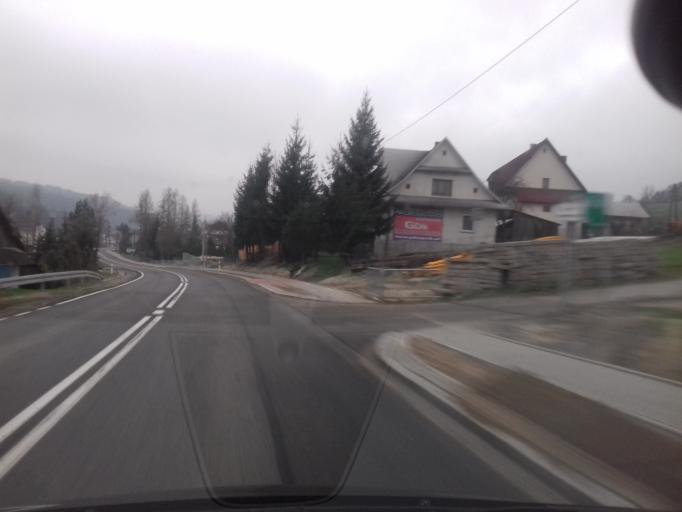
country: PL
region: Lesser Poland Voivodeship
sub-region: Powiat limanowski
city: Kasina Wielka
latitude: 49.6962
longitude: 20.1223
